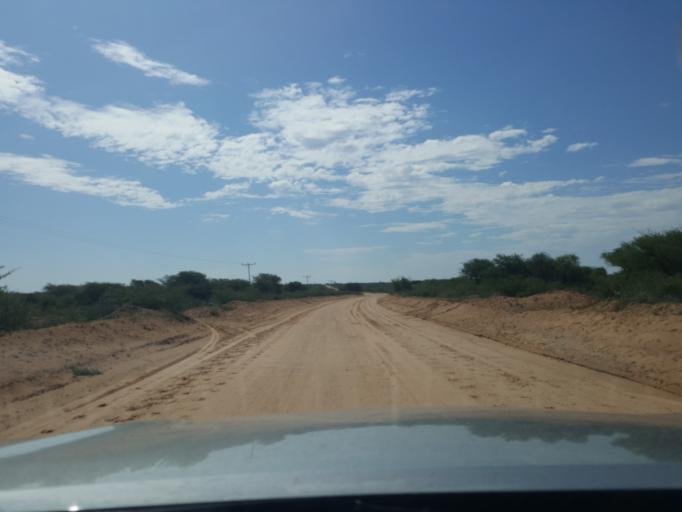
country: BW
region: Kweneng
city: Khudumelapye
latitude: -23.8848
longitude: 24.9110
